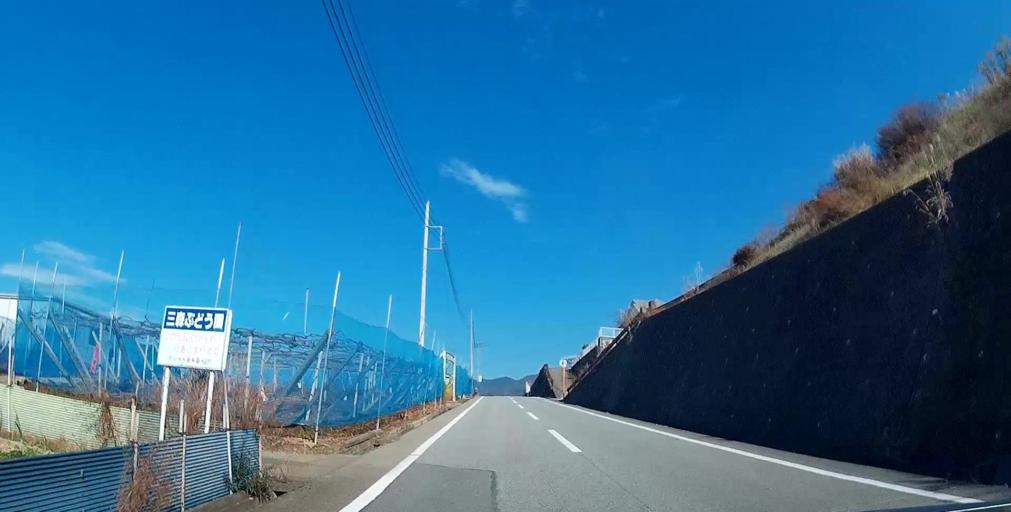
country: JP
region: Yamanashi
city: Enzan
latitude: 35.6683
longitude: 138.7437
